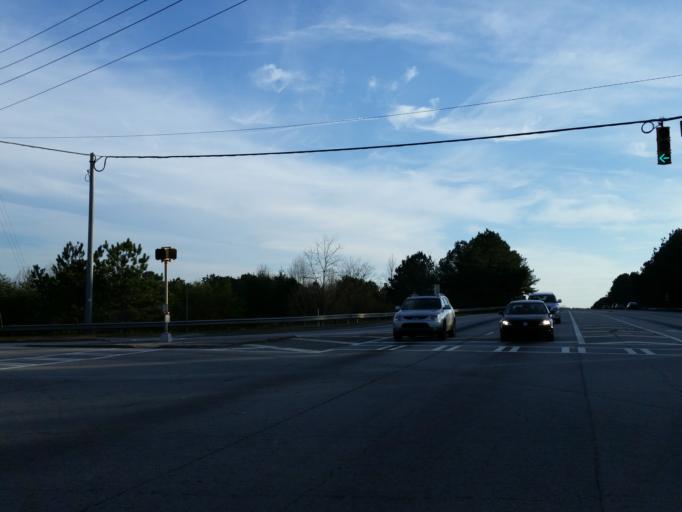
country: US
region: Georgia
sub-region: Cobb County
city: Powder Springs
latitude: 33.8676
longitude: -84.6969
